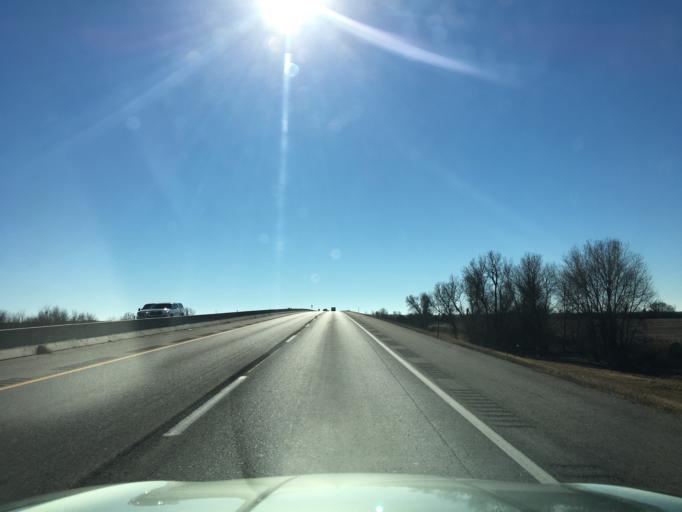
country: US
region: Kansas
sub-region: Sumner County
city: Wellington
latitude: 37.0763
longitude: -97.3386
